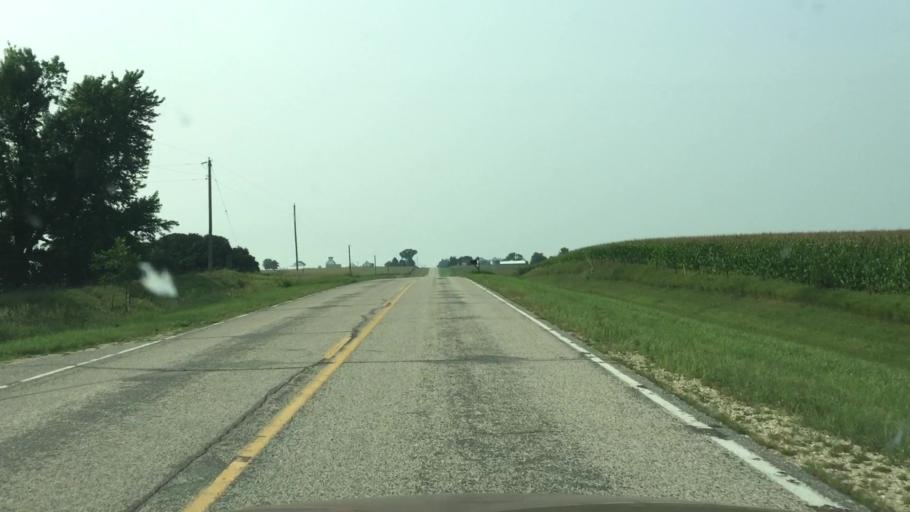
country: US
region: Iowa
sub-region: O'Brien County
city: Sheldon
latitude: 43.2775
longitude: -95.7829
